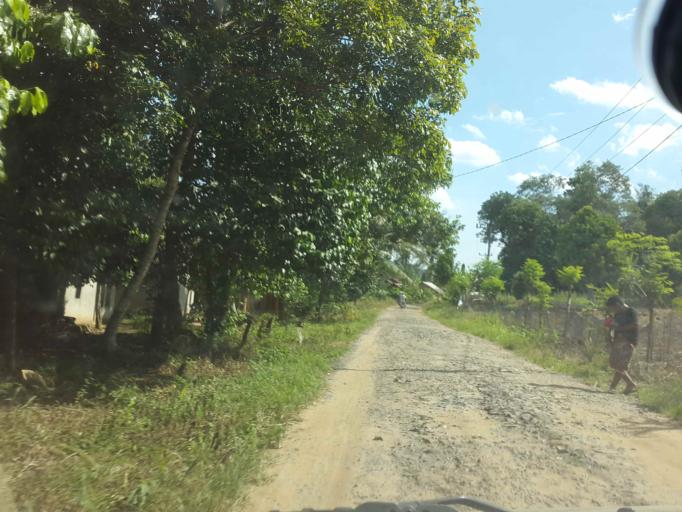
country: ID
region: Lampung
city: Panjang
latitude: -5.4151
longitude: 105.3573
